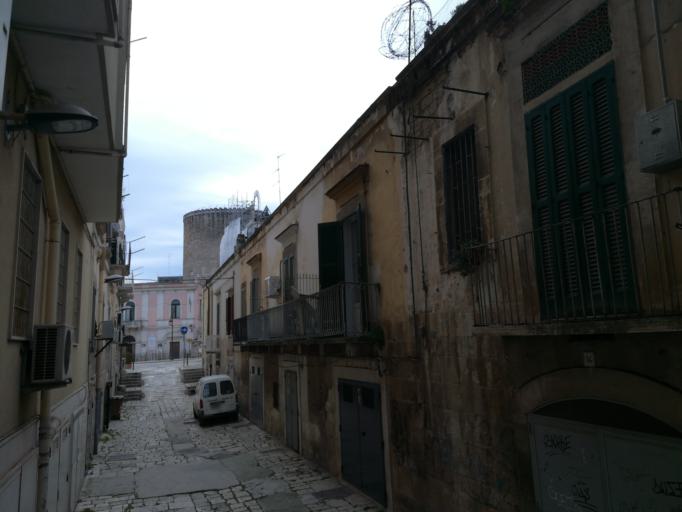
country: IT
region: Apulia
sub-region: Provincia di Bari
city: Bitonto
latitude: 41.1083
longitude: 16.6908
